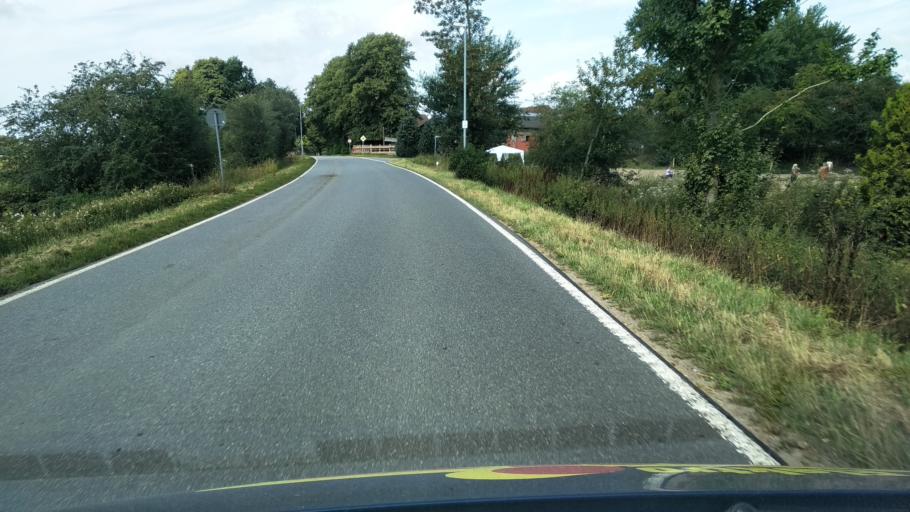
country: DE
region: Schleswig-Holstein
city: Brekendorf
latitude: 54.4223
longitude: 9.6270
